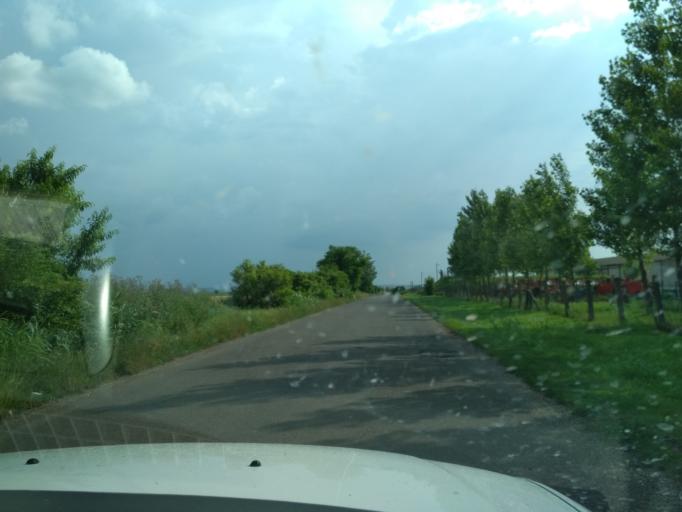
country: HU
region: Pest
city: Tapioszentmarton
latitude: 47.3284
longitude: 19.7326
